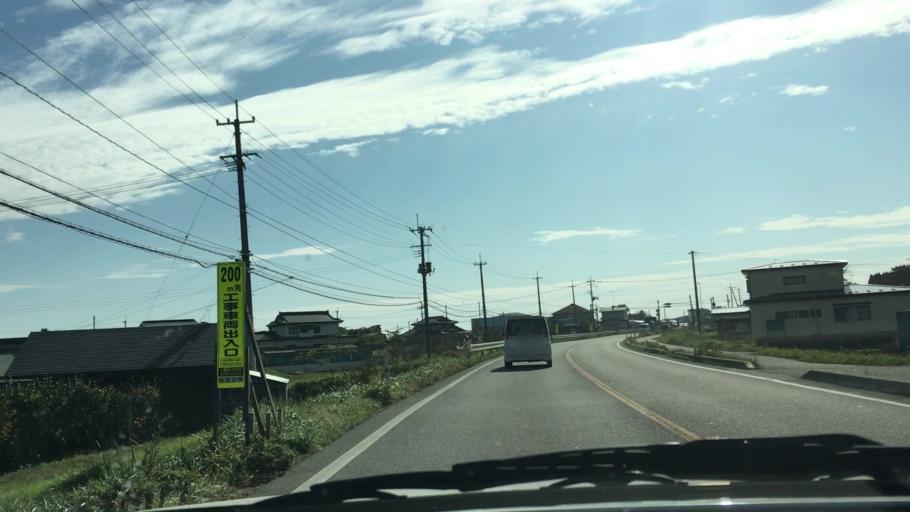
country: JP
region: Aomori
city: Hachinohe
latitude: 40.4248
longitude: 141.6975
